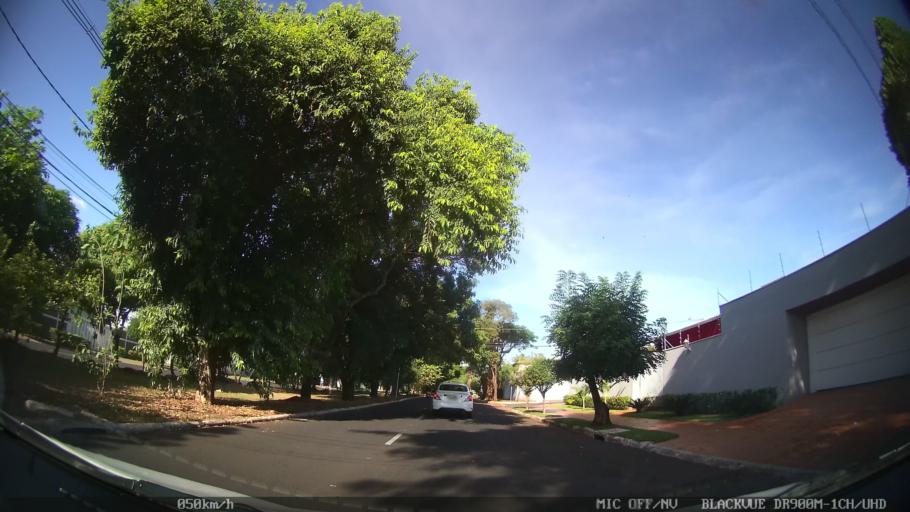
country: BR
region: Sao Paulo
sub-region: Ribeirao Preto
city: Ribeirao Preto
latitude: -21.1898
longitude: -47.7660
